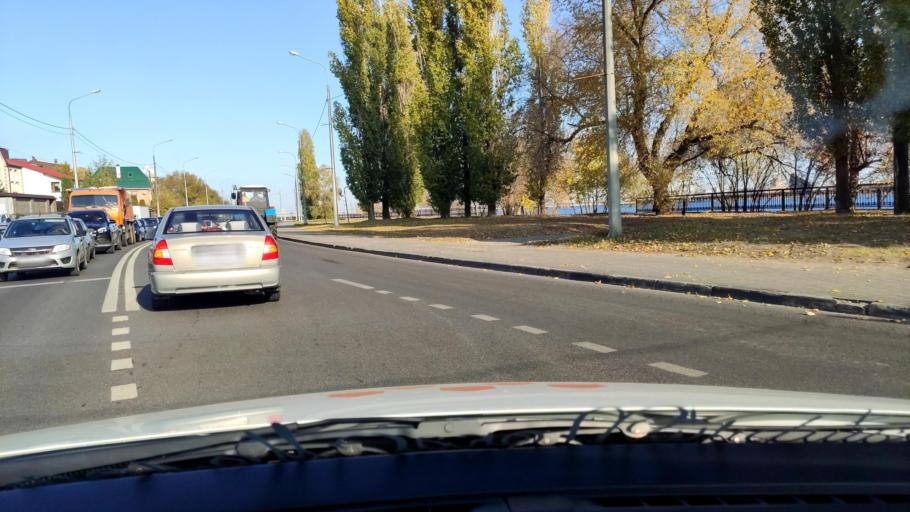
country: RU
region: Voronezj
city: Voronezh
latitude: 51.6787
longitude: 39.2271
